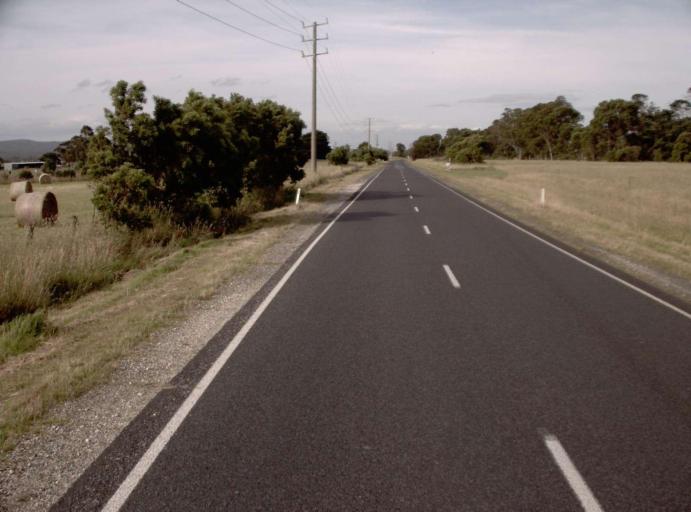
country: AU
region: Victoria
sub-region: Latrobe
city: Traralgon
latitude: -38.1012
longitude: 146.5940
